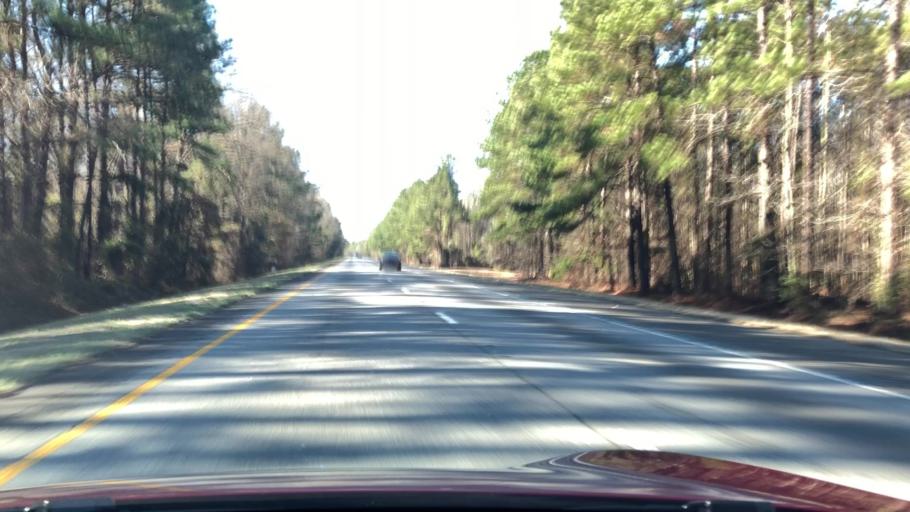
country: US
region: South Carolina
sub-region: Clarendon County
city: Manning
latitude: 33.5604
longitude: -80.3972
